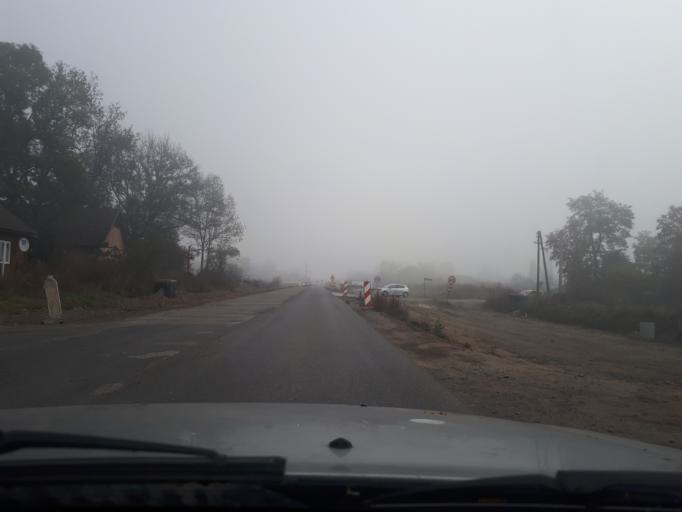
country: PL
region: Lesser Poland Voivodeship
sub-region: Powiat wielicki
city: Podleze
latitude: 50.0769
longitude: 20.1541
